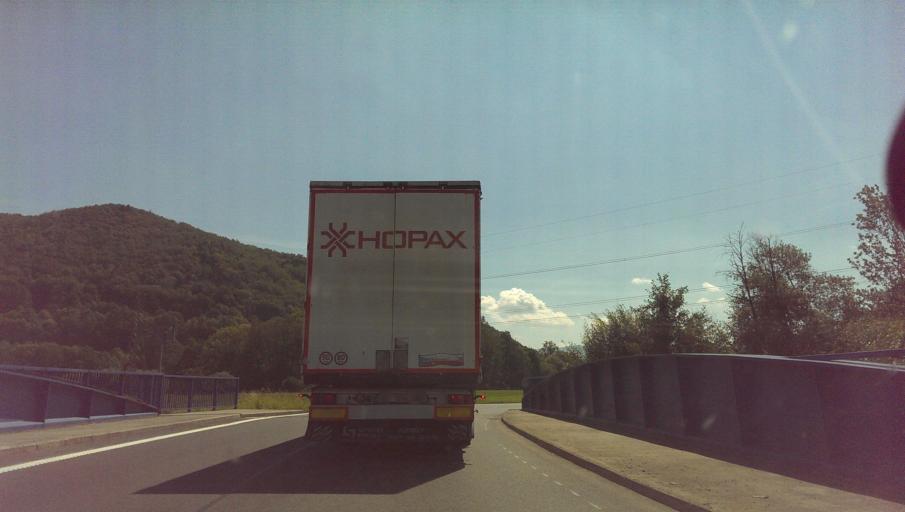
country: CZ
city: Lichnov (o. Novy Jicin)
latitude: 49.5862
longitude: 18.1908
